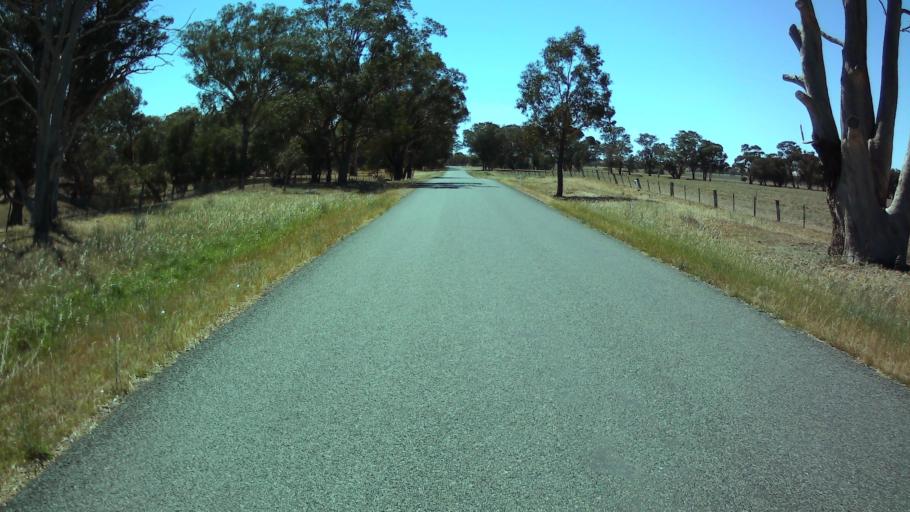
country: AU
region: New South Wales
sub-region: Weddin
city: Grenfell
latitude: -34.0022
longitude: 148.3785
